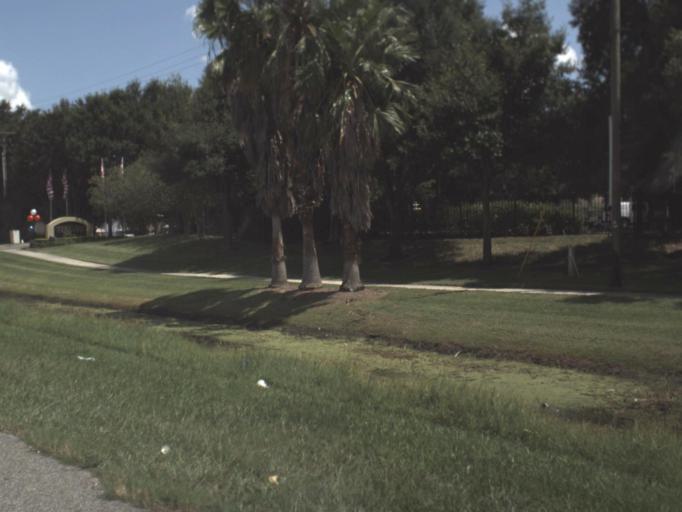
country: US
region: Florida
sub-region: Hillsborough County
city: Brandon
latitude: 27.9232
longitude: -82.3009
